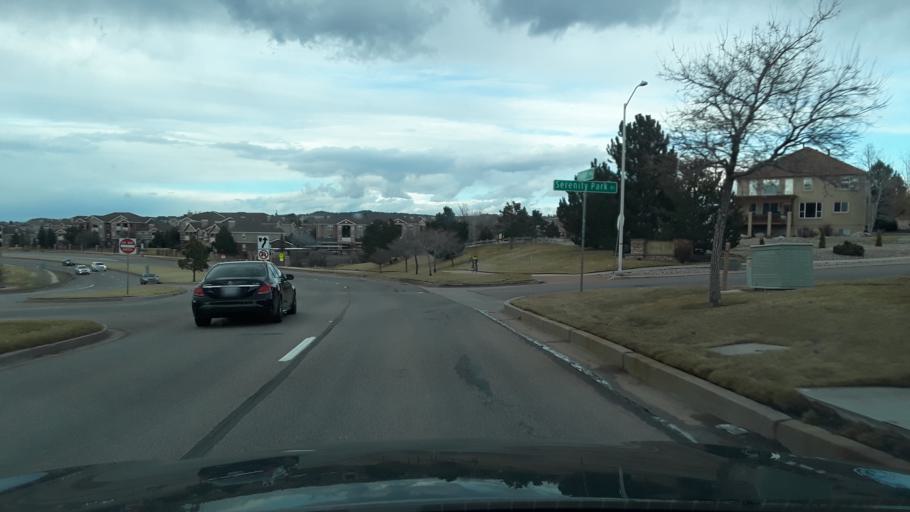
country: US
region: Colorado
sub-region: El Paso County
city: Gleneagle
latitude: 39.0155
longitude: -104.8085
